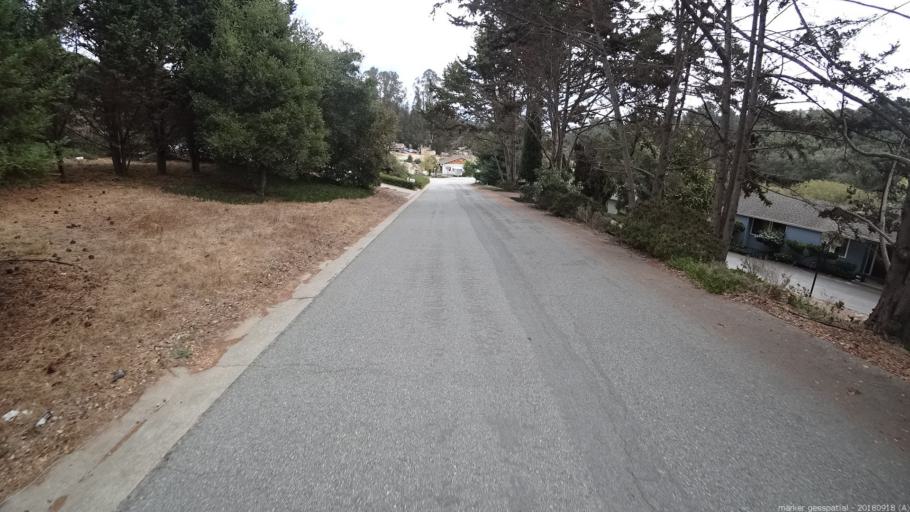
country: US
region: California
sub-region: Monterey County
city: Prunedale
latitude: 36.7955
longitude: -121.6592
